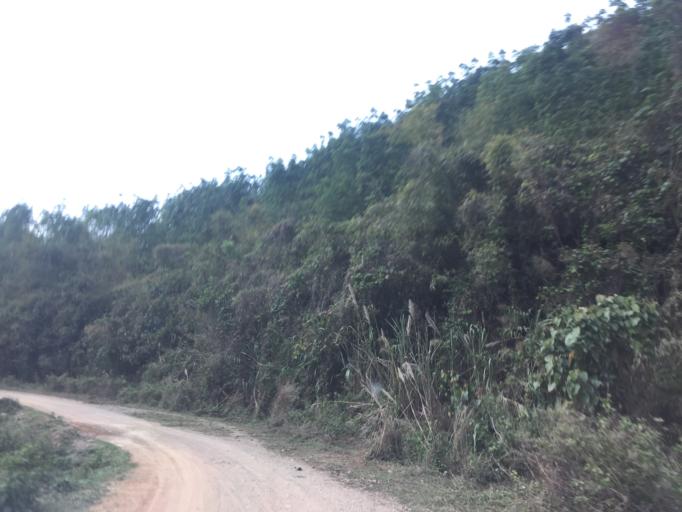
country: TH
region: Nan
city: Song Khwae
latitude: 19.7412
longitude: 100.7134
